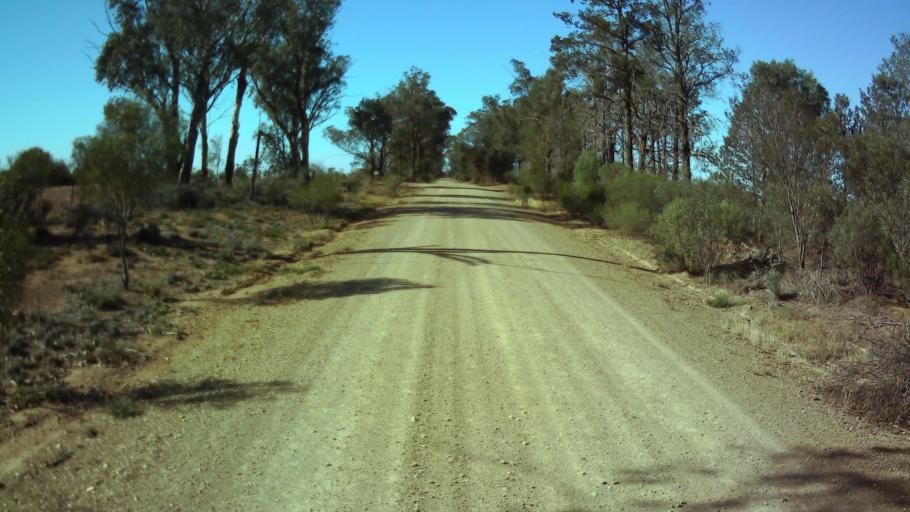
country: AU
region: New South Wales
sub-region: Weddin
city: Grenfell
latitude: -33.9061
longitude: 147.8776
